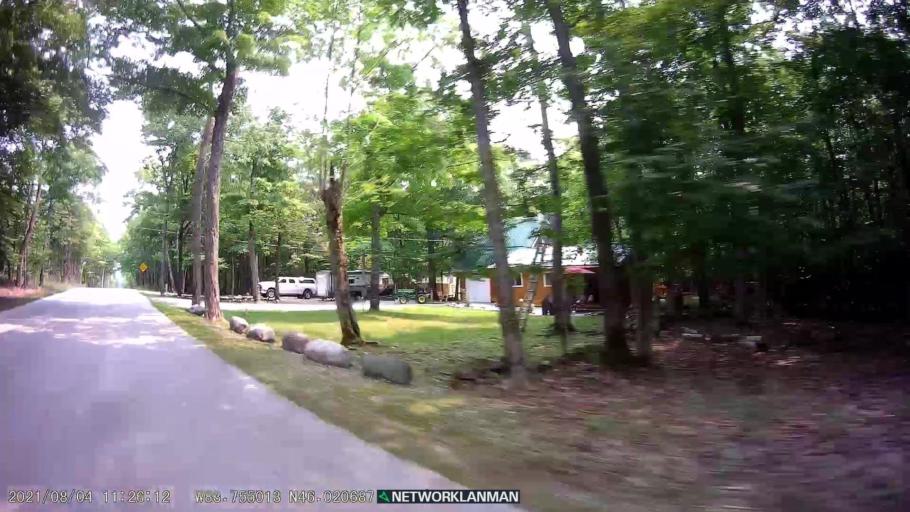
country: CA
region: Ontario
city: Thessalon
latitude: 46.0207
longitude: -83.7543
